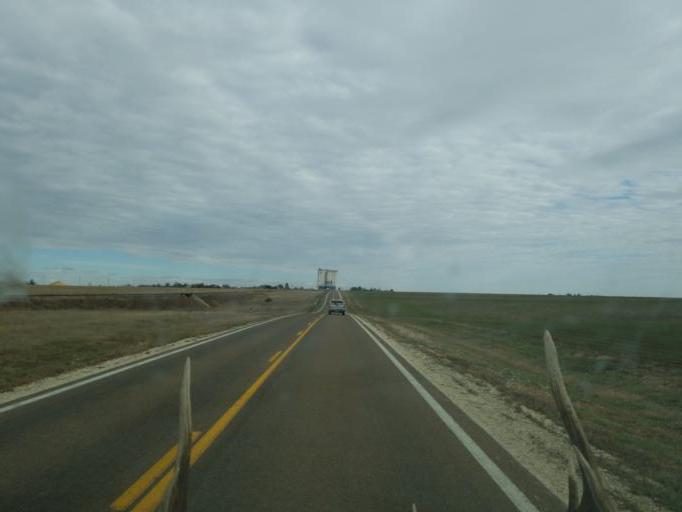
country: US
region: Kansas
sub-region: Logan County
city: Oakley
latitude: 39.0859
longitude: -101.1643
